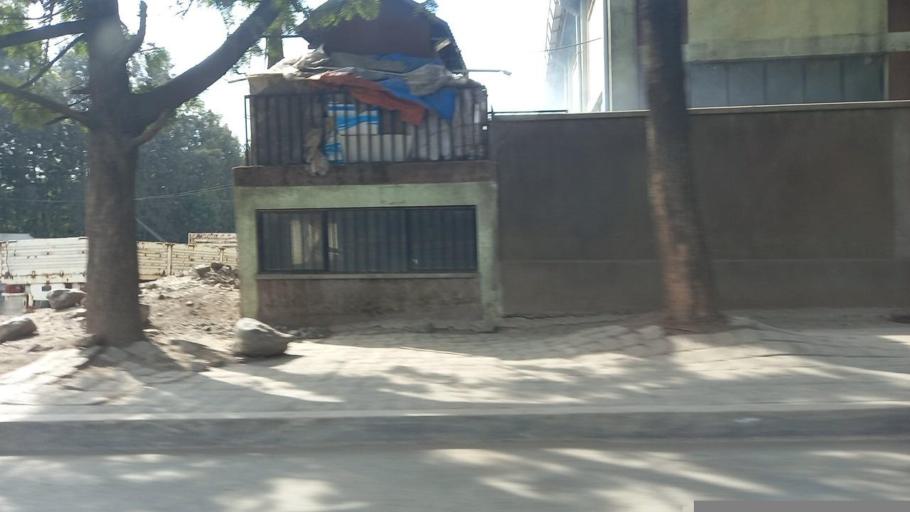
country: ET
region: Adis Abeba
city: Addis Ababa
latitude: 9.0065
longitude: 38.8196
